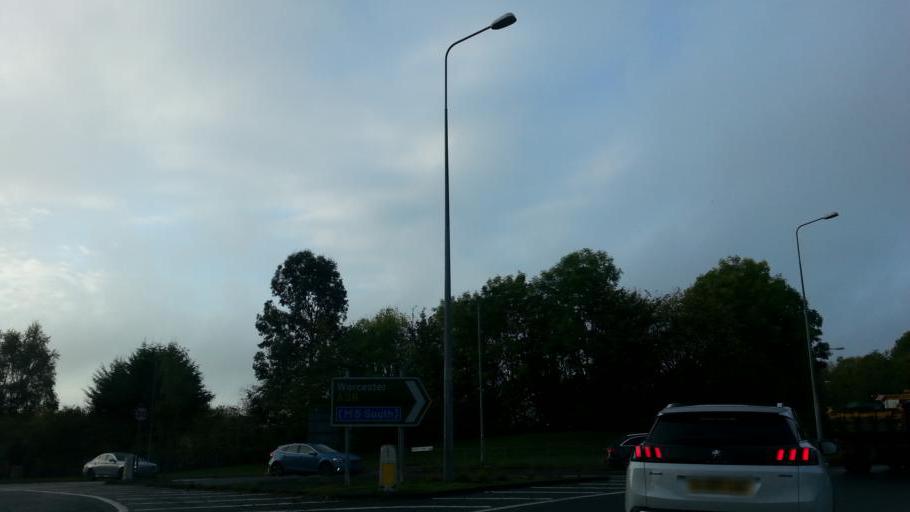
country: GB
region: England
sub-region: Worcestershire
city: Bromsgrove
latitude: 52.3346
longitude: -2.0466
